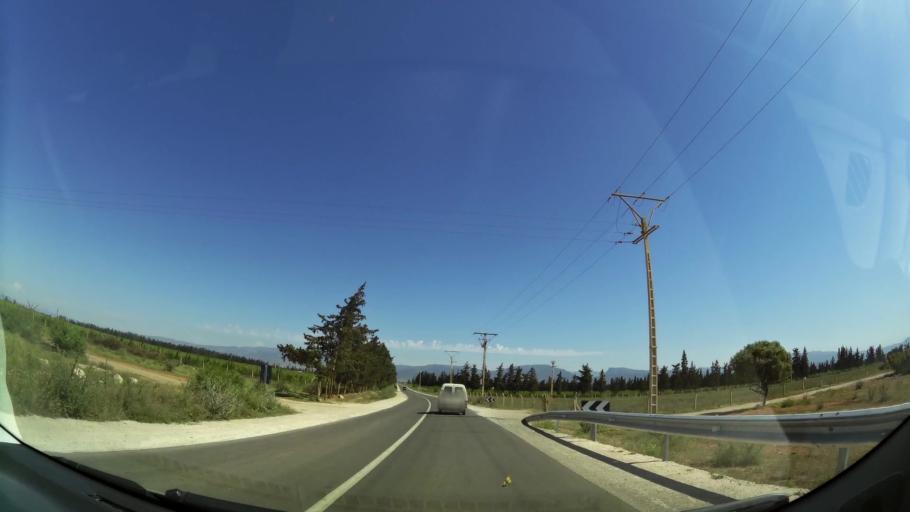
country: MA
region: Oriental
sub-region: Berkane-Taourirt
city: Madagh
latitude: 34.9925
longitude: -2.3924
